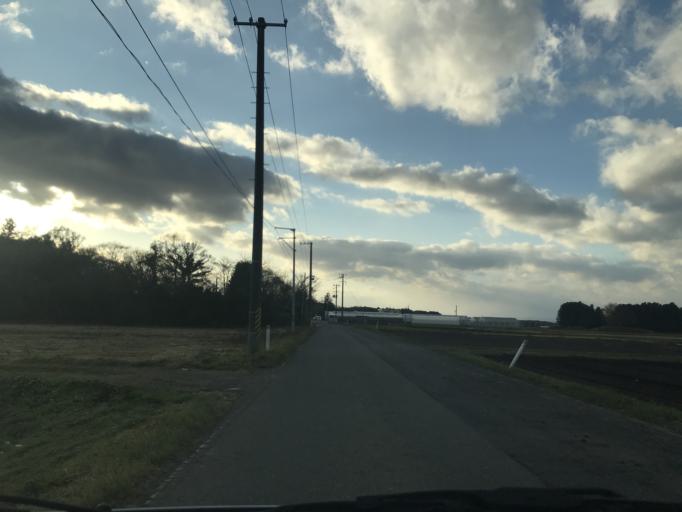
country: JP
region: Miyagi
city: Kogota
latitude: 38.6338
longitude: 141.0581
